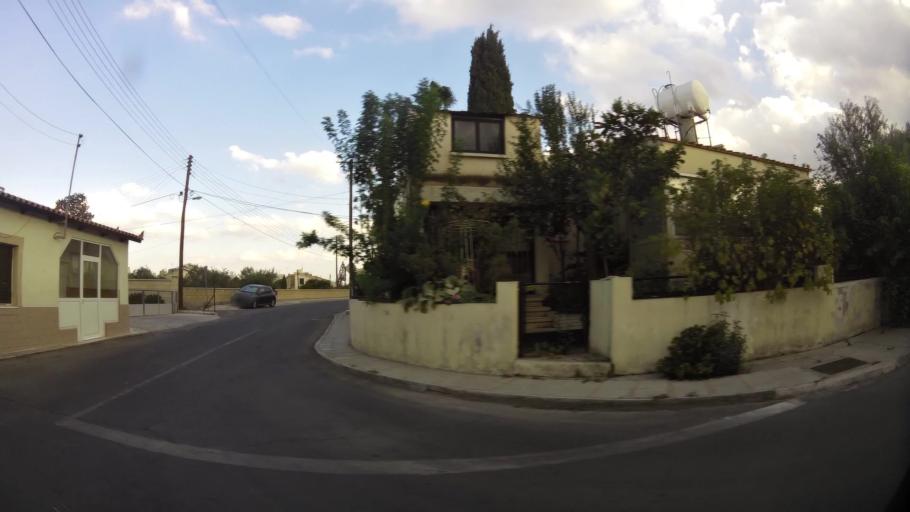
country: CY
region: Lefkosia
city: Kato Deftera
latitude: 35.1169
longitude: 33.3016
